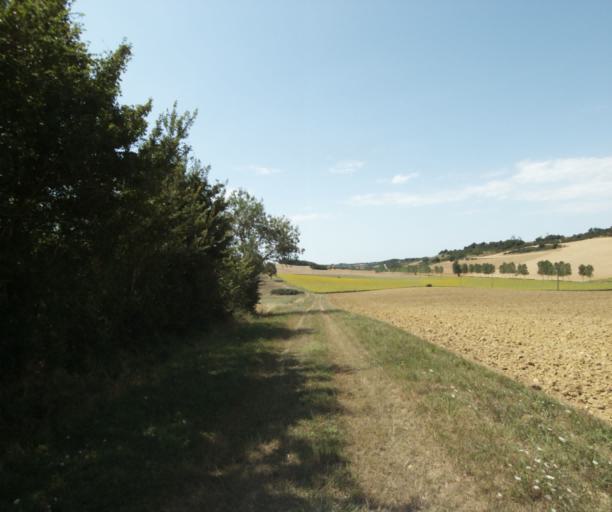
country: FR
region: Midi-Pyrenees
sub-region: Departement de la Haute-Garonne
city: Saint-Felix-Lauragais
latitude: 43.4560
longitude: 1.8754
